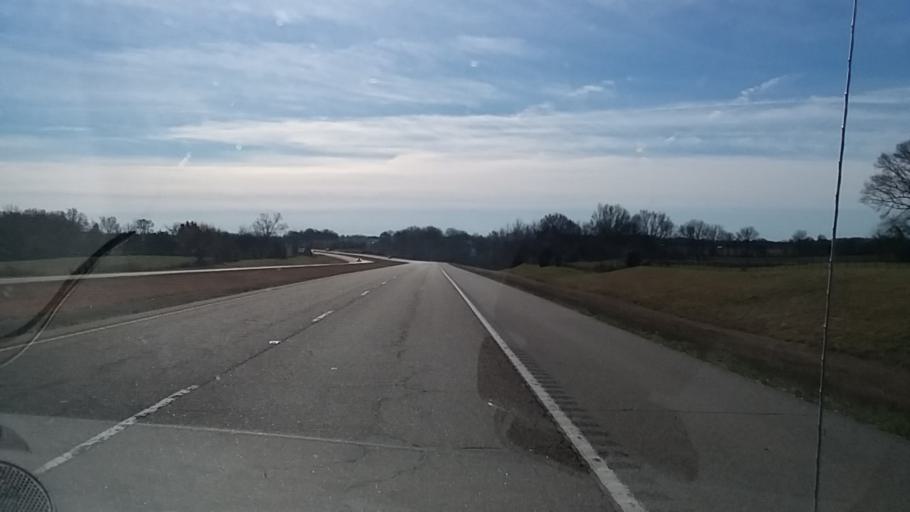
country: US
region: Tennessee
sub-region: Crockett County
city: Alamo
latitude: 35.7805
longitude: -89.1404
